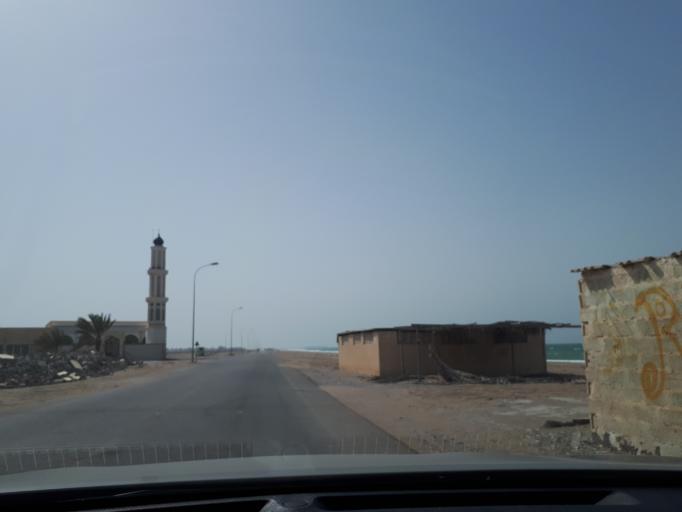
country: OM
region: Al Batinah
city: Barka'
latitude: 23.7208
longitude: 57.8546
